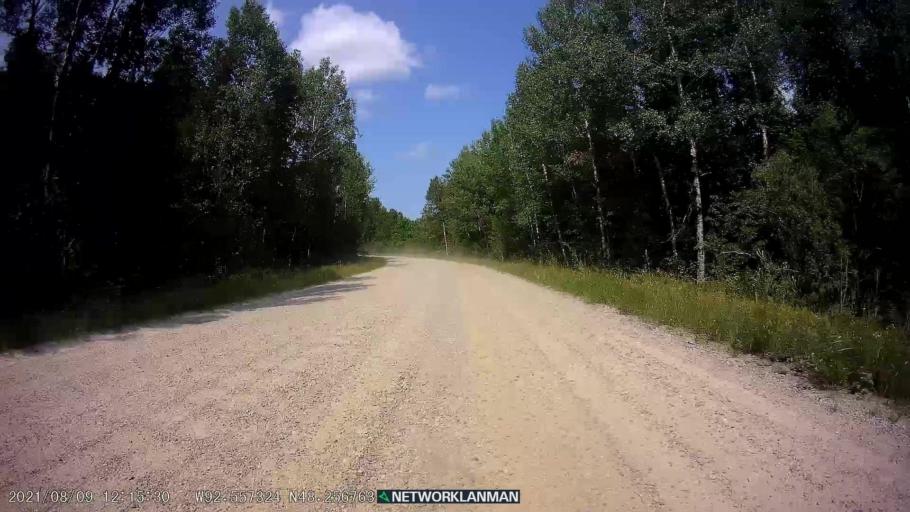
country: US
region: Minnesota
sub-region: Saint Louis County
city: Parkville
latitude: 48.2568
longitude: -92.5573
